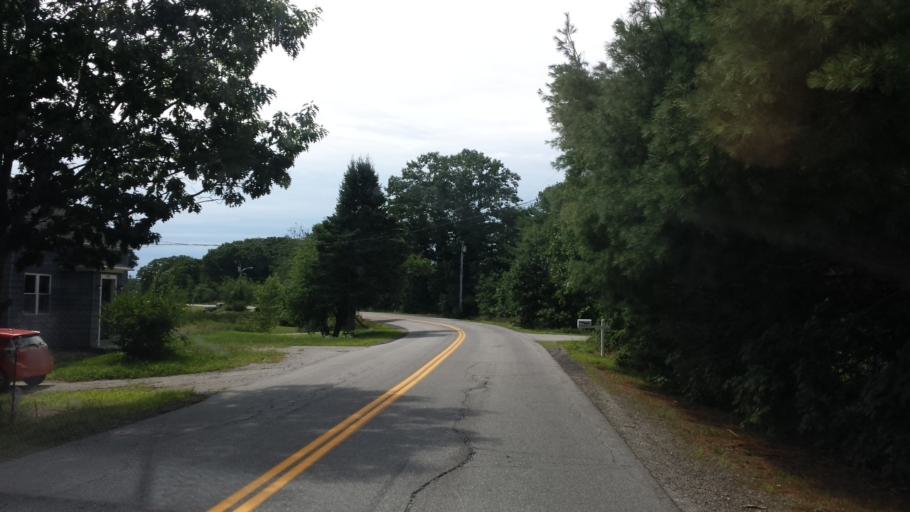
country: US
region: Maine
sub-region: York County
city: Biddeford
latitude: 43.4358
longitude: -70.4079
